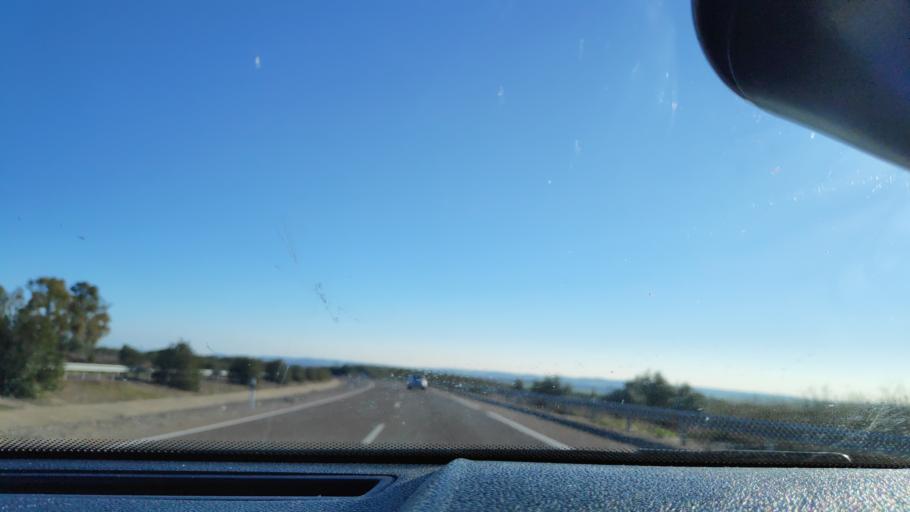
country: ES
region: Andalusia
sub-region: Provincia de Sevilla
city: Guillena
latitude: 37.5565
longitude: -6.1038
